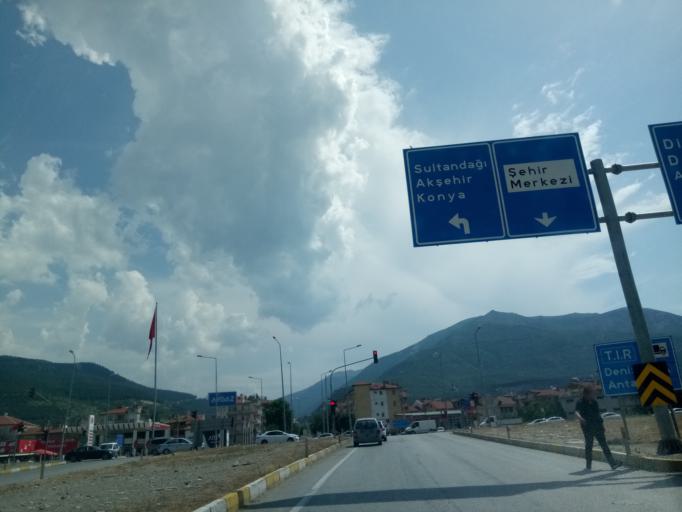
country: TR
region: Afyonkarahisar
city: Cay
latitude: 38.5978
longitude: 31.0289
